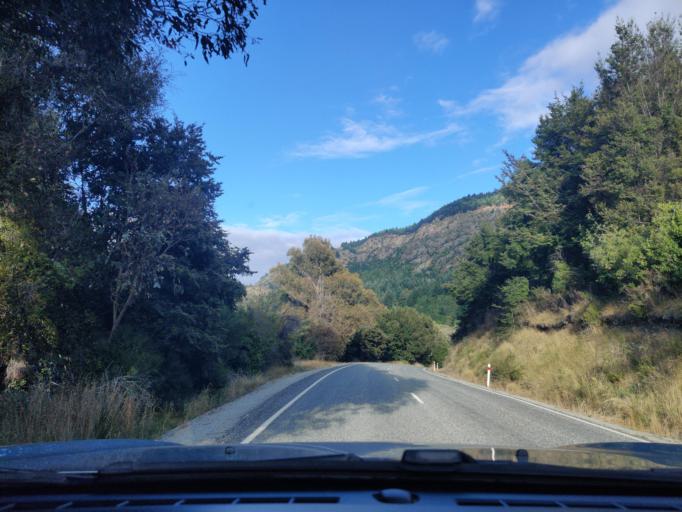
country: NZ
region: Otago
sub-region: Queenstown-Lakes District
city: Queenstown
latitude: -45.0468
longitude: 168.6283
